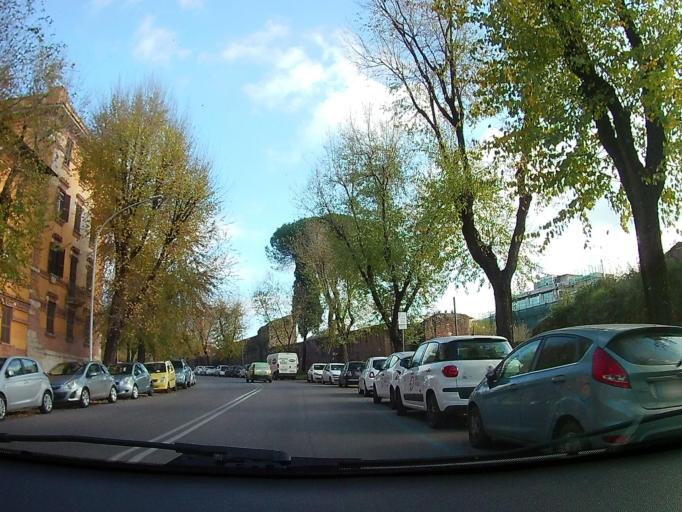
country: IT
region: Latium
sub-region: Citta metropolitana di Roma Capitale
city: Rome
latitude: 41.8771
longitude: 12.4845
